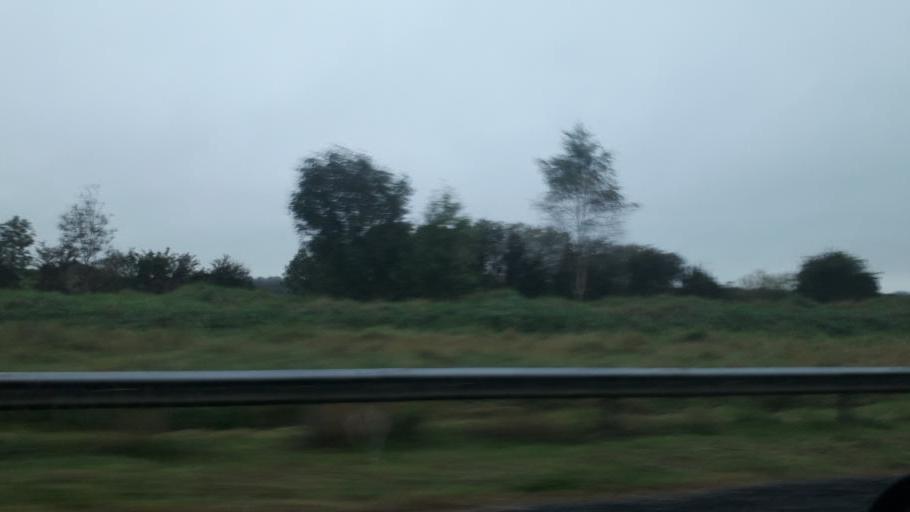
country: IE
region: Leinster
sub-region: An Iarmhi
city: Rochfortbridge
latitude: 53.5077
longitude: -7.2467
